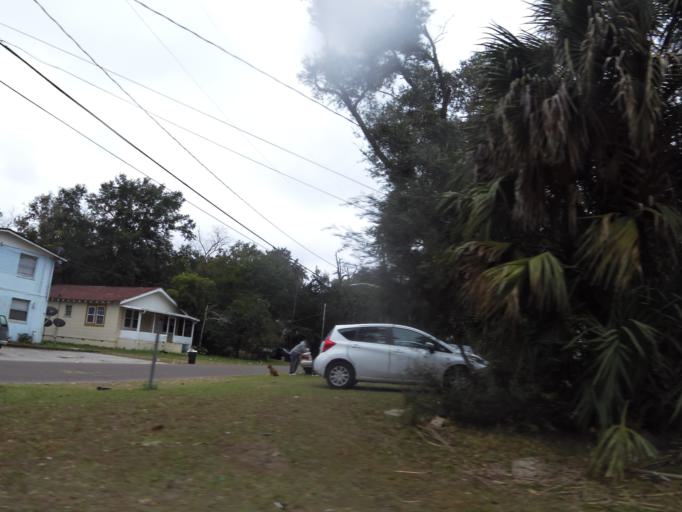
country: US
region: Florida
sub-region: Duval County
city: Jacksonville
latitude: 30.3671
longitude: -81.6835
